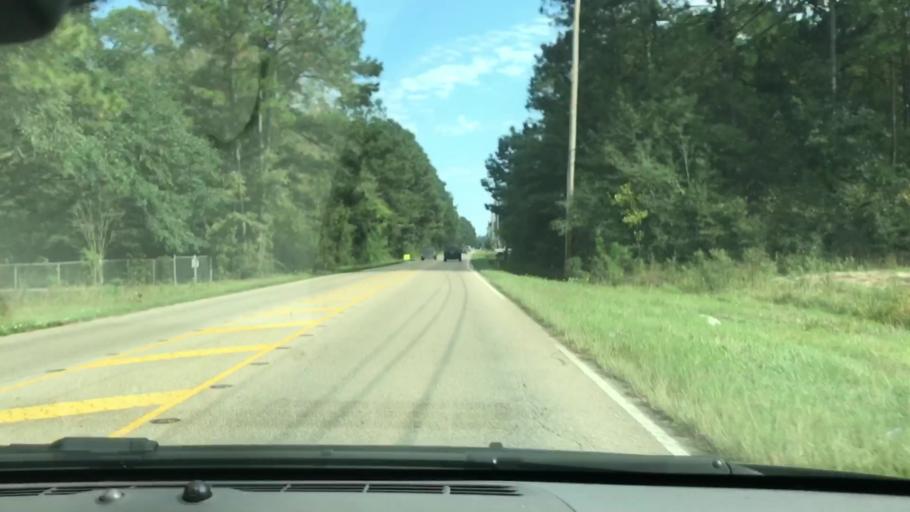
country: US
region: Louisiana
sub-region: Saint Tammany Parish
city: Abita Springs
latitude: 30.4599
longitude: -90.0599
